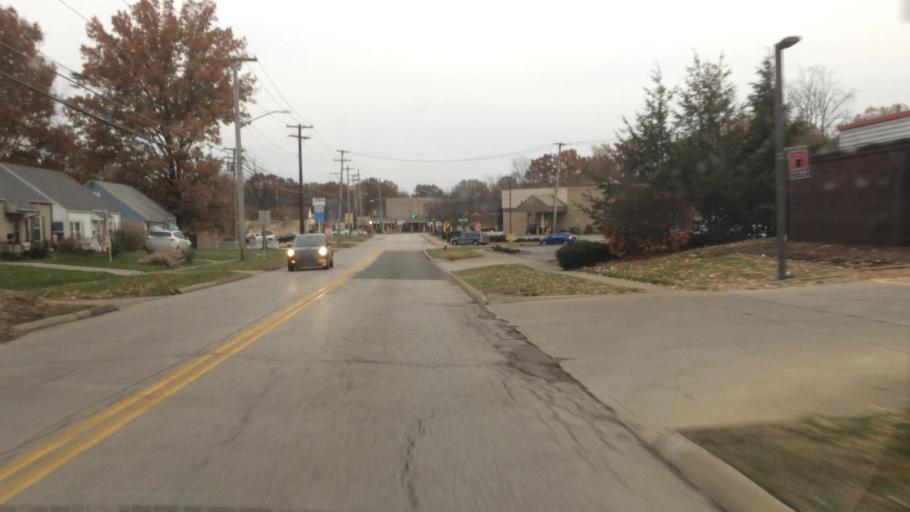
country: US
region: Ohio
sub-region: Summit County
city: Cuyahoga Falls
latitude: 41.1339
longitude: -81.4671
